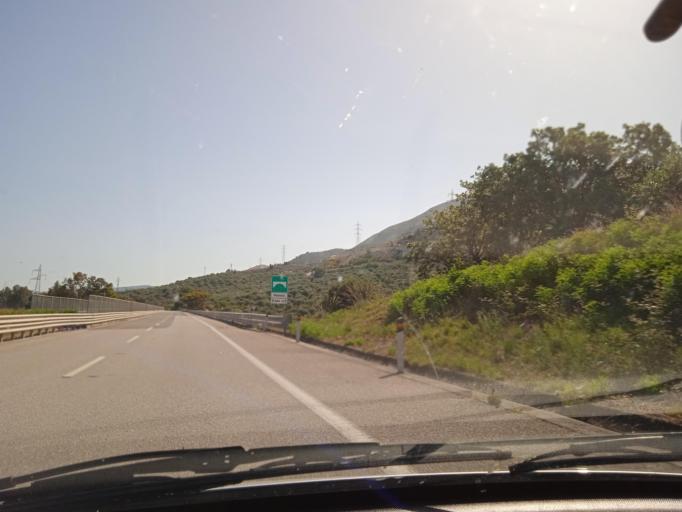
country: IT
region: Sicily
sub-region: Messina
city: Torrenova
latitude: 38.0845
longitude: 14.6880
